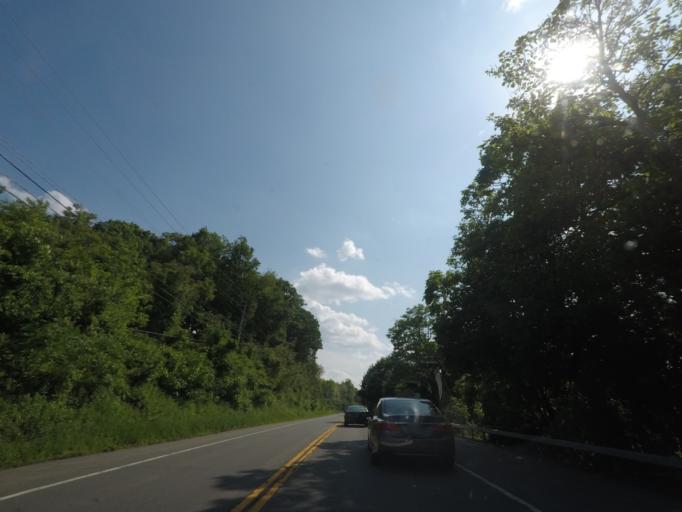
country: US
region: New York
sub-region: Orange County
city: Balmville
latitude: 41.5696
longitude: -73.9933
